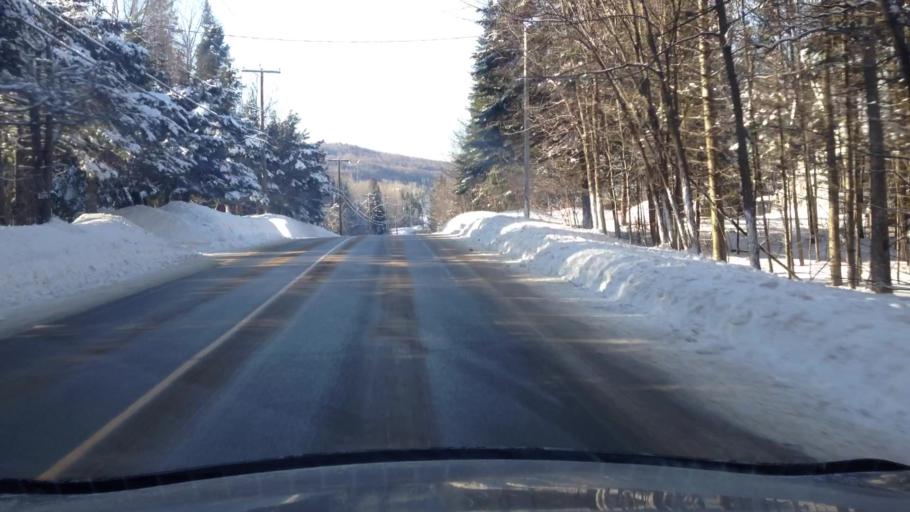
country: CA
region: Quebec
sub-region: Laurentides
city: Sainte-Agathe-des-Monts
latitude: 45.9298
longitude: -74.4123
